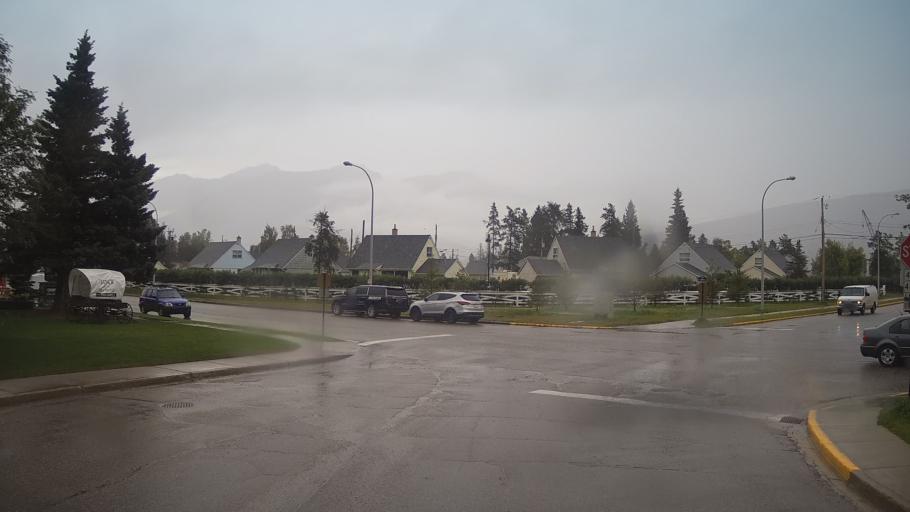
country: CA
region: Alberta
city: Jasper Park Lodge
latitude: 52.8842
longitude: -118.0816
